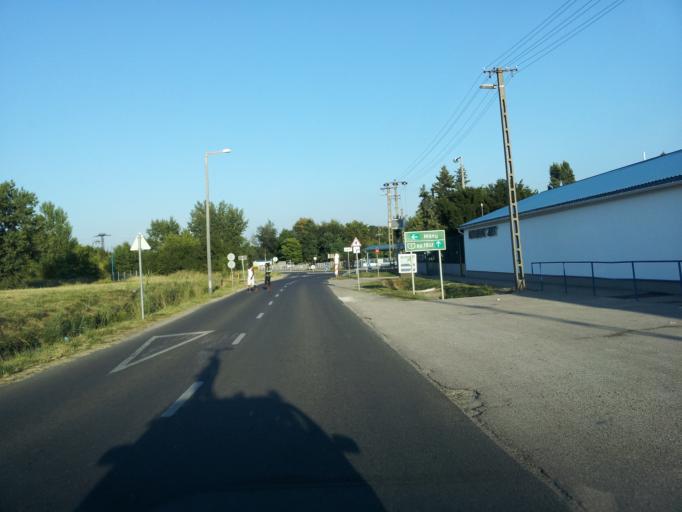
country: HU
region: Fejer
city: Bicske
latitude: 47.5013
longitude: 18.6288
